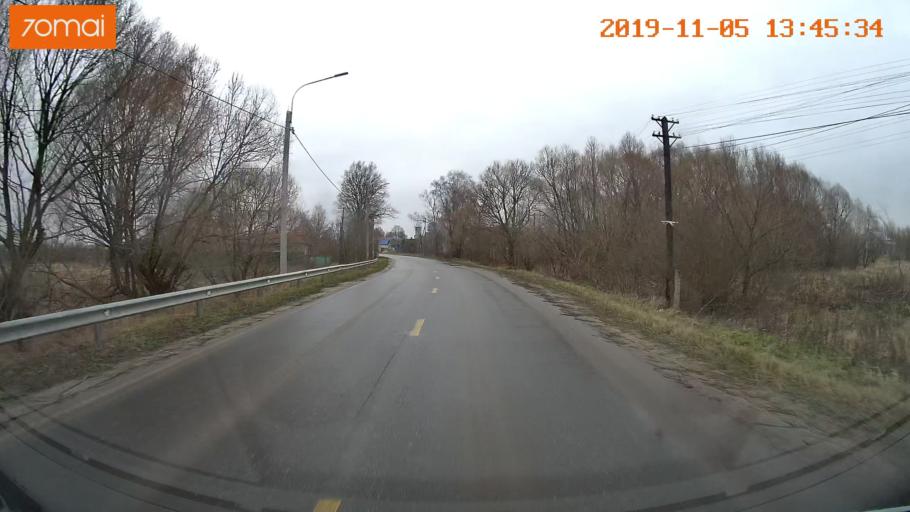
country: RU
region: Ivanovo
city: Shuya
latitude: 56.9897
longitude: 41.4123
